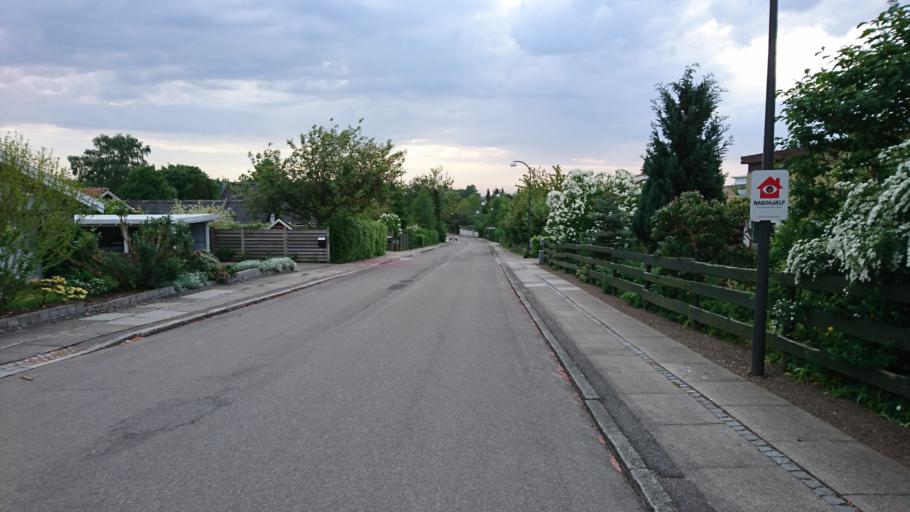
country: DK
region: Capital Region
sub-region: Fureso Kommune
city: Vaerlose
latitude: 55.7546
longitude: 12.3981
